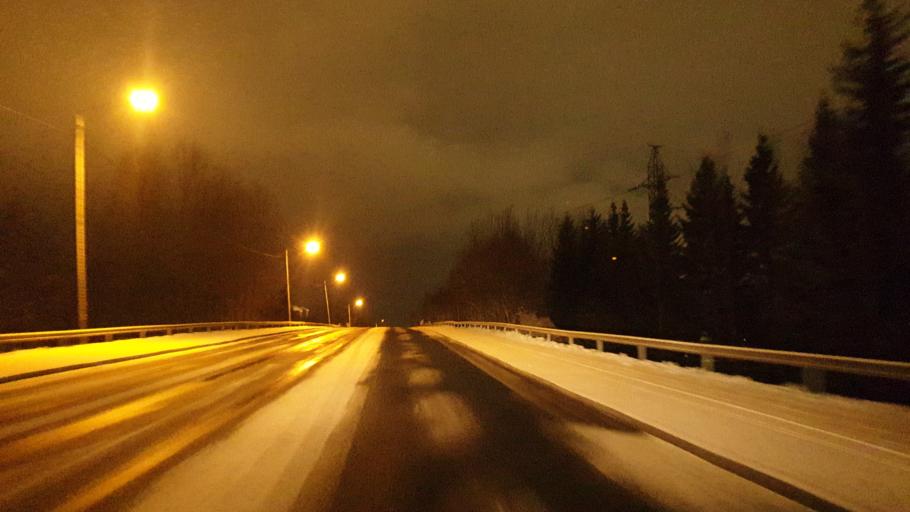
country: FI
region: Northern Ostrobothnia
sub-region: Oulu
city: Oulu
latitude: 64.9879
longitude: 25.4712
